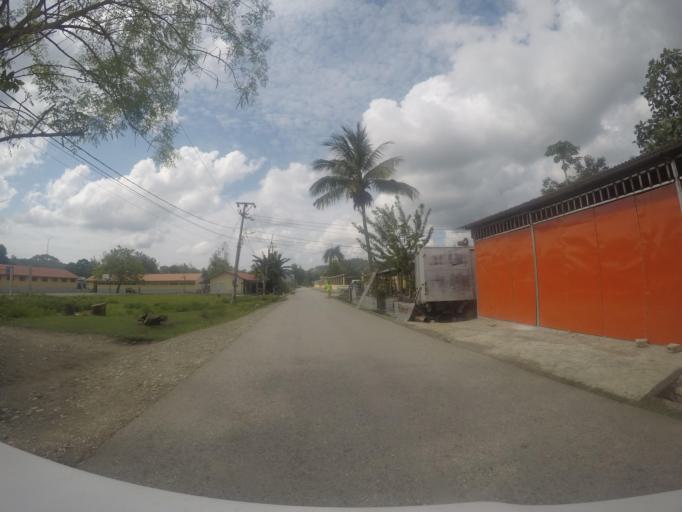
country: TL
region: Viqueque
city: Viqueque
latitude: -8.8550
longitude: 126.3638
